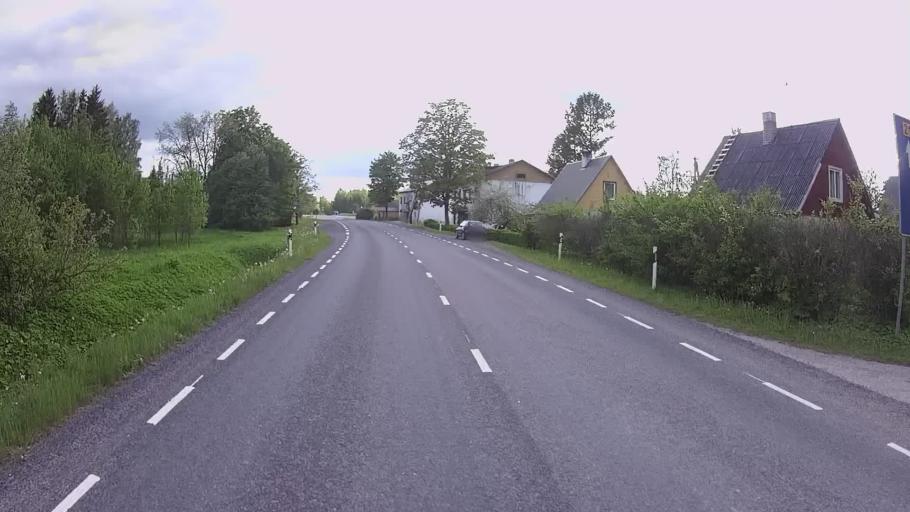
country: EE
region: Jogevamaa
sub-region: Mustvee linn
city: Mustvee
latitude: 58.9808
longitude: 26.8320
